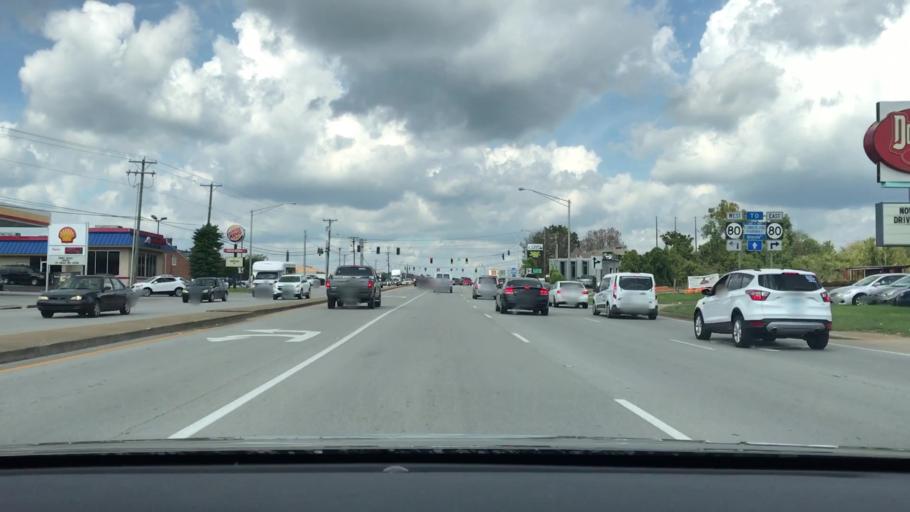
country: US
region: Kentucky
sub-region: Pulaski County
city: Somerset
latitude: 37.0926
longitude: -84.6181
